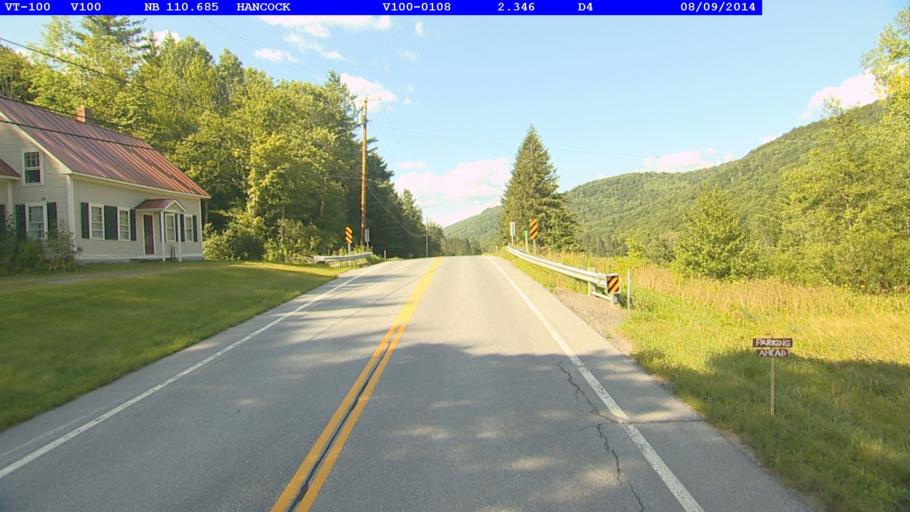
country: US
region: Vermont
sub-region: Orange County
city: Randolph
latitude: 43.9424
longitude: -72.8413
